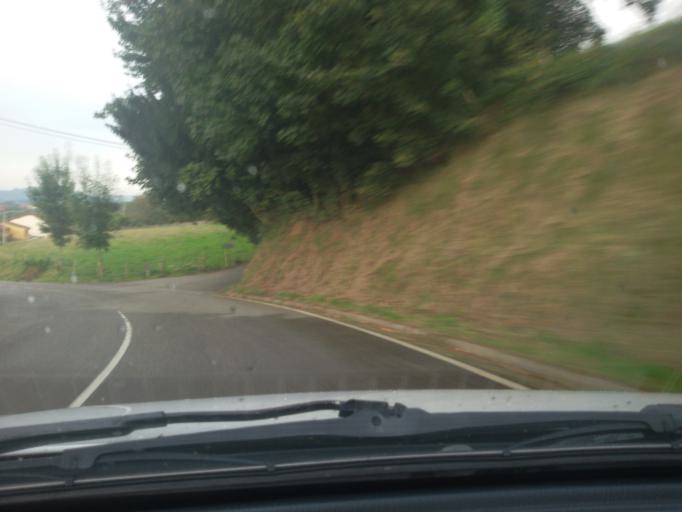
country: ES
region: Asturias
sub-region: Province of Asturias
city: Norena
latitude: 43.3676
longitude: -5.7458
